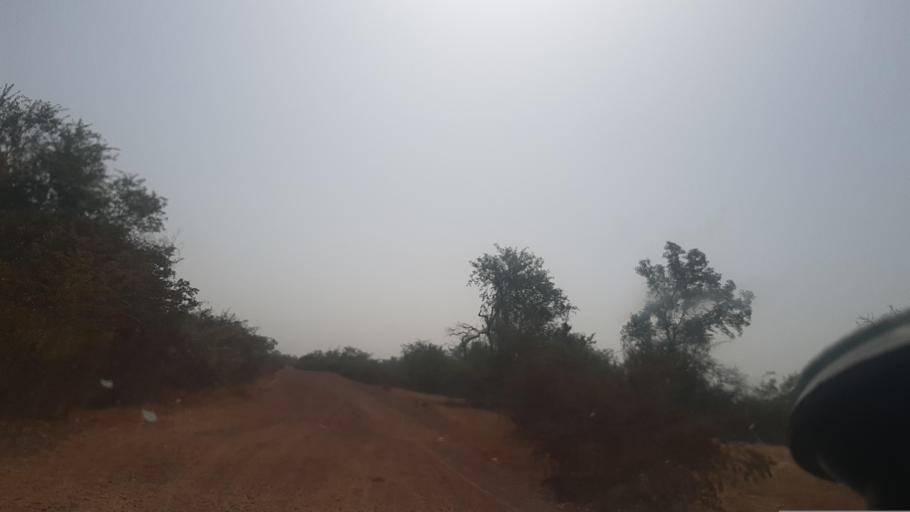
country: ML
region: Segou
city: Baroueli
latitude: 13.0661
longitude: -6.4775
